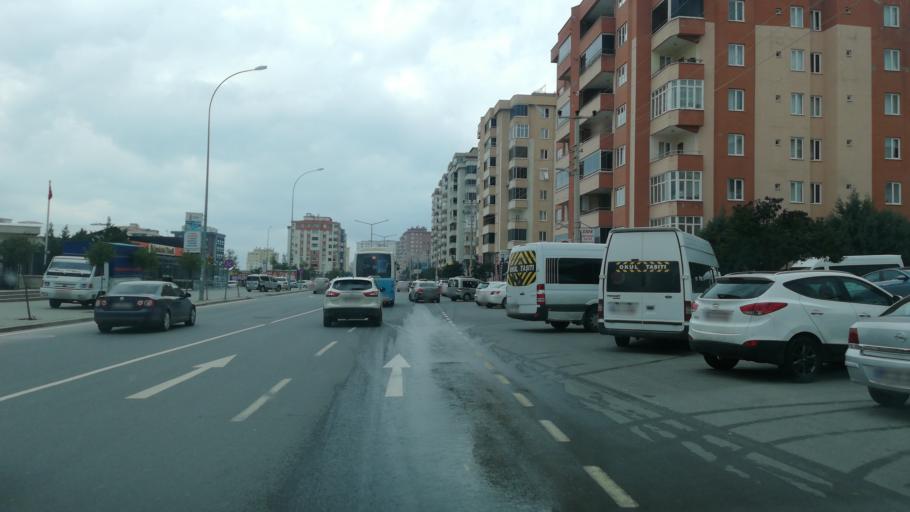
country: TR
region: Kahramanmaras
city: Kahramanmaras
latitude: 37.5834
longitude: 36.8688
